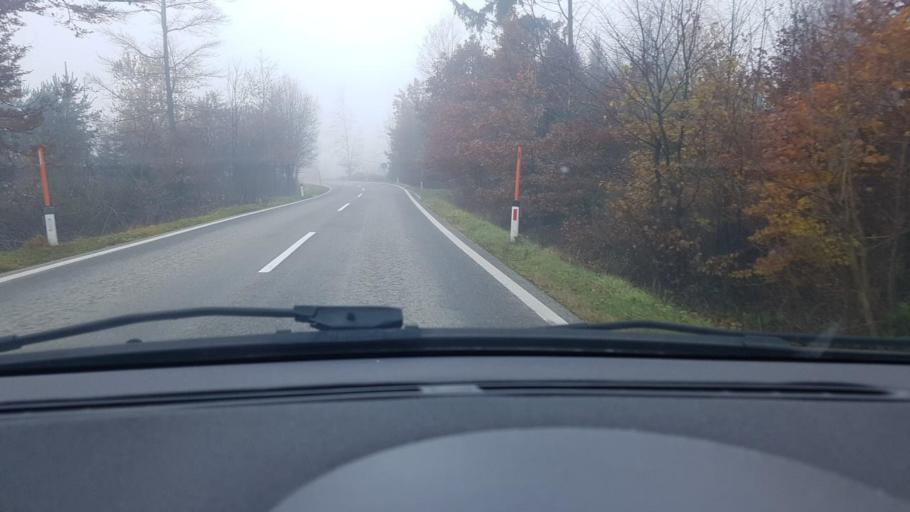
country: AT
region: Carinthia
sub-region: Politischer Bezirk Volkermarkt
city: Sittersdorf
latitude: 46.5485
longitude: 14.6210
